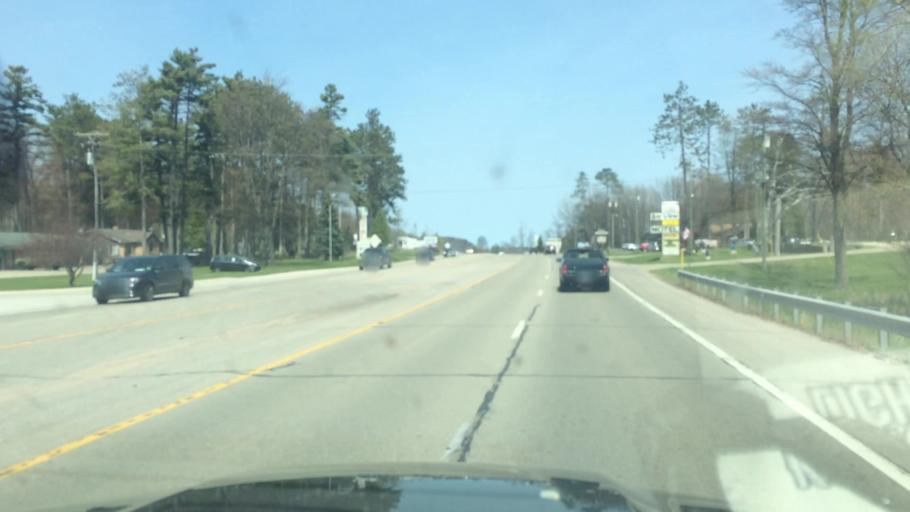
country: US
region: Michigan
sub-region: Delta County
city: Escanaba
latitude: 45.8039
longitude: -87.0636
